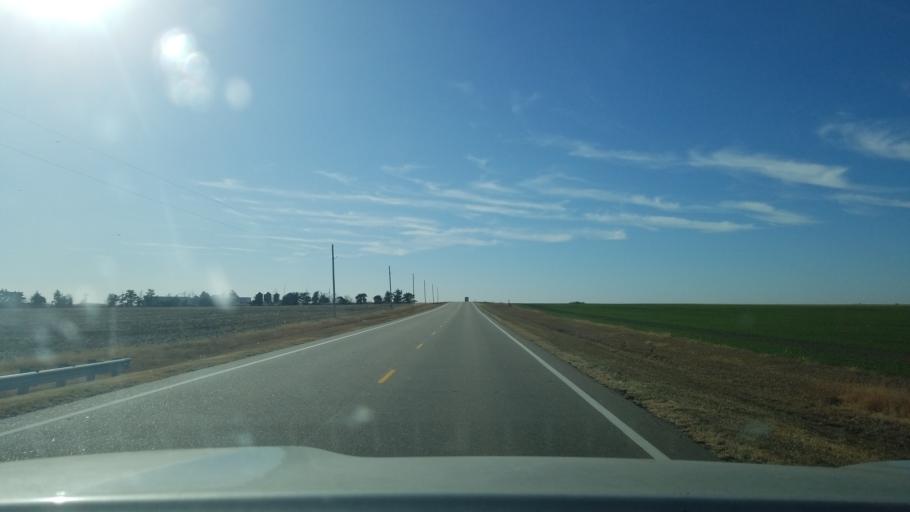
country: US
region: Kansas
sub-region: Ness County
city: Ness City
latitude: 38.3882
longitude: -99.8982
